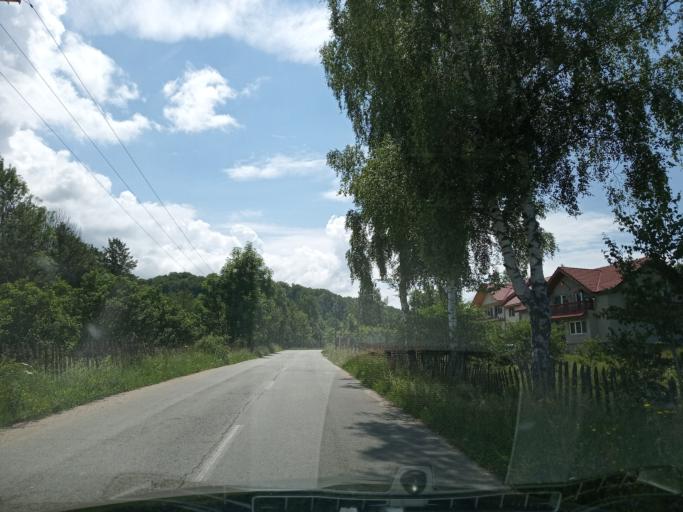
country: RO
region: Hunedoara
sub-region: Oras Petrila
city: Petrila
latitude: 45.4161
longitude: 23.4112
